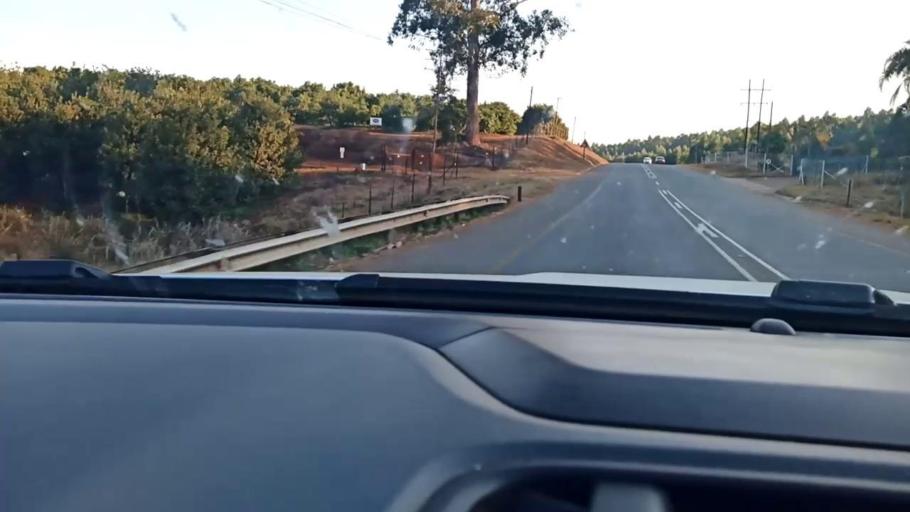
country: ZA
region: Limpopo
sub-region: Mopani District Municipality
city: Duiwelskloof
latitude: -23.7129
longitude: 30.1289
